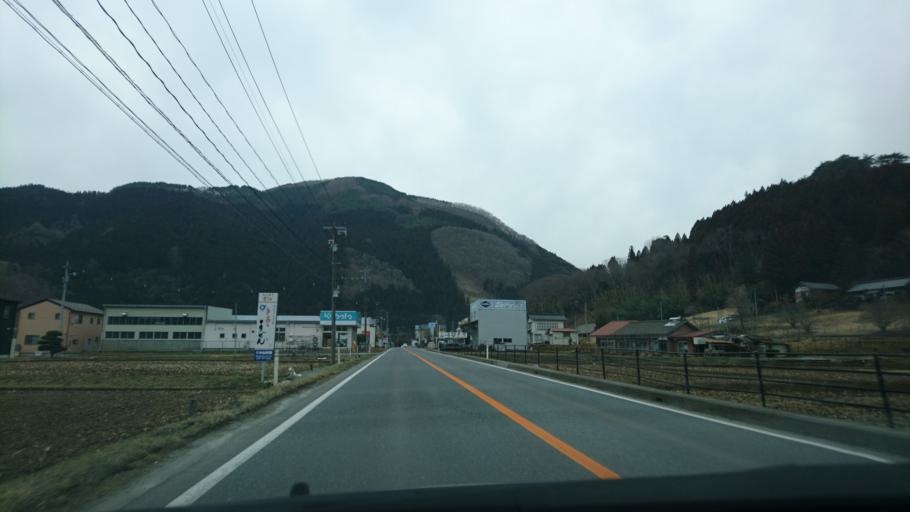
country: JP
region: Iwate
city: Tono
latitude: 39.1442
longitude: 141.5535
